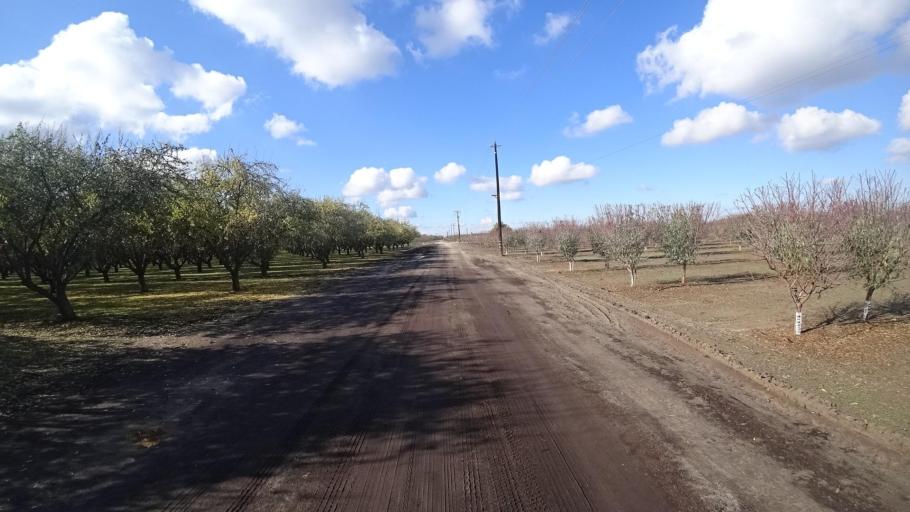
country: US
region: California
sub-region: Kern County
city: McFarland
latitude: 35.6526
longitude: -119.2351
